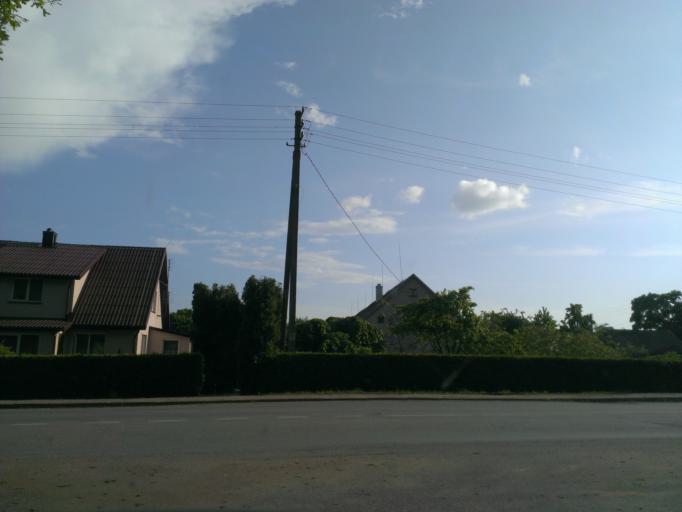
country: LT
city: Salantai
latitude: 56.0713
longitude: 21.4063
